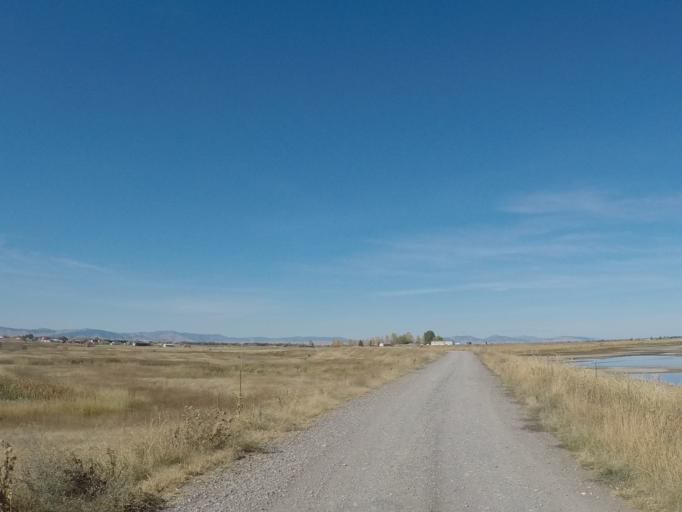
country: US
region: Montana
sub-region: Lake County
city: Ronan
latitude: 47.4539
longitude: -114.0834
